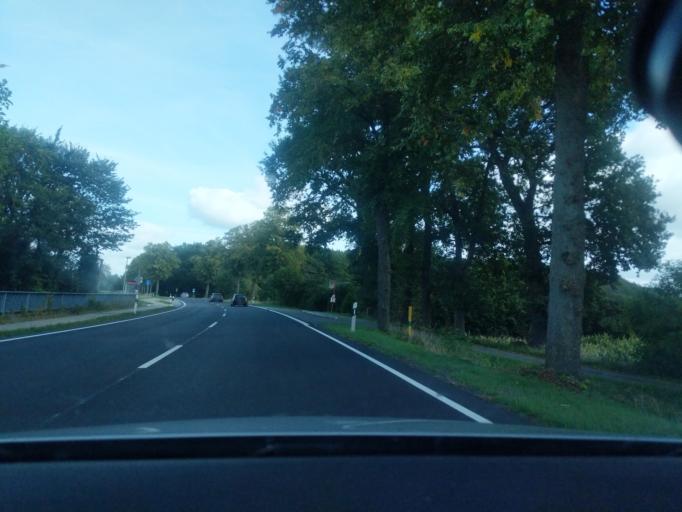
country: DE
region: Lower Saxony
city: Belm
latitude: 52.3286
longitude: 8.1653
